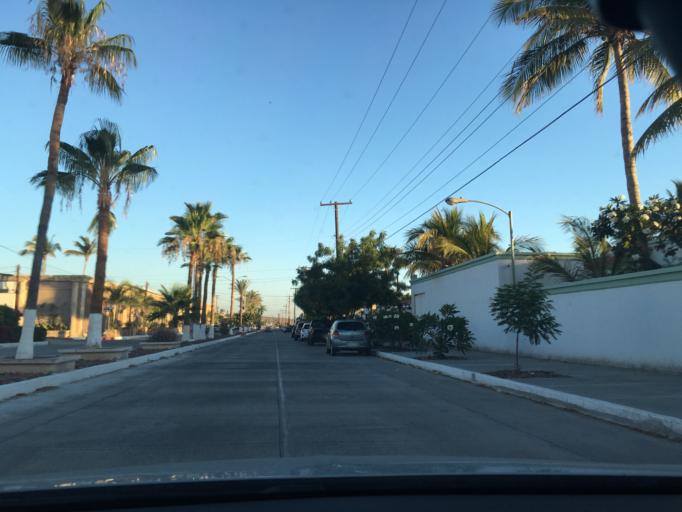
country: MX
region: Baja California Sur
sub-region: La Paz
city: La Paz
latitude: 24.1254
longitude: -110.3080
